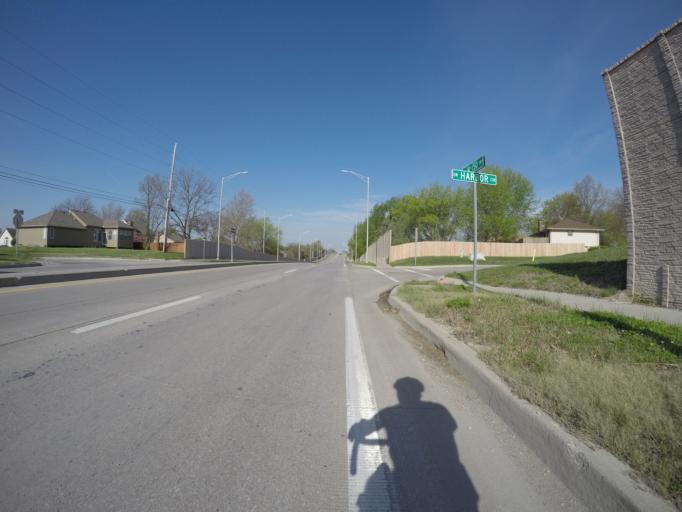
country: US
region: Missouri
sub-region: Cass County
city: Lake Winnebago
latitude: 38.8532
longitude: -94.3898
